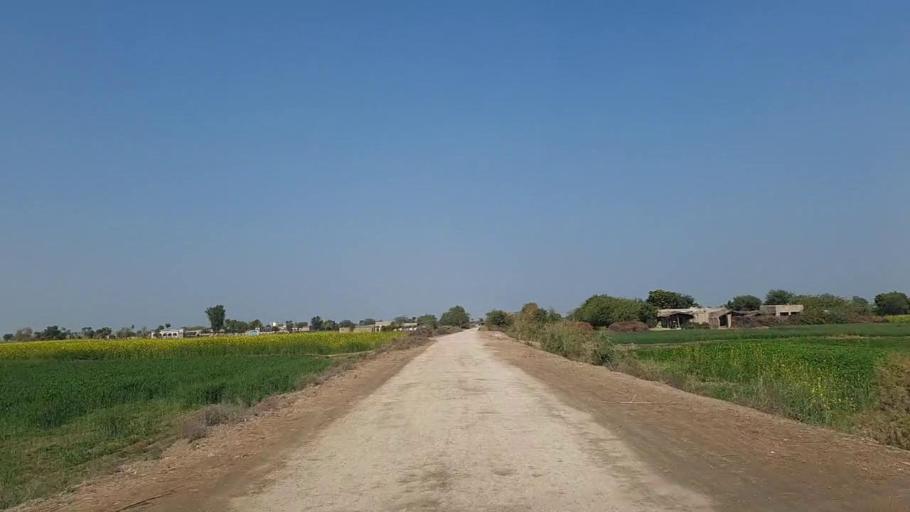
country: PK
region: Sindh
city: Nawabshah
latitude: 26.2768
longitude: 68.5135
